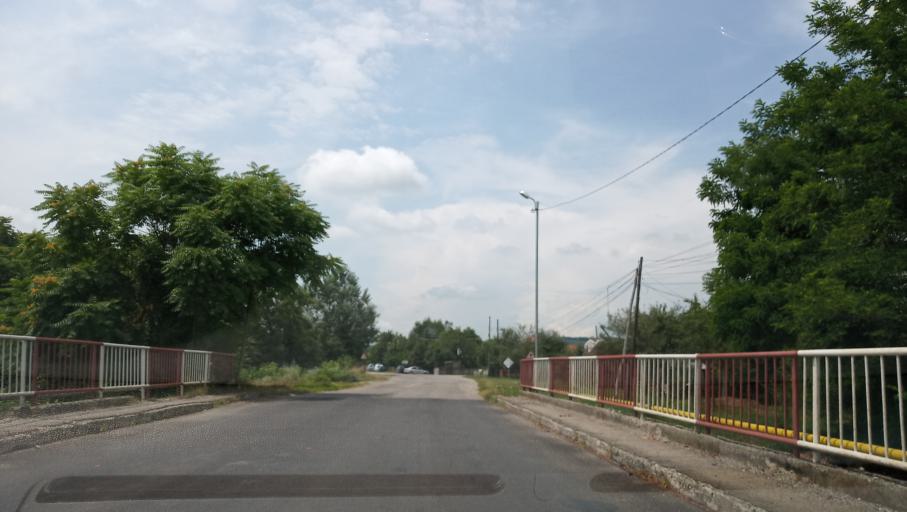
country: RO
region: Gorj
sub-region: Comuna Turcinesti
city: Turcinesti
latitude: 45.1099
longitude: 23.3191
